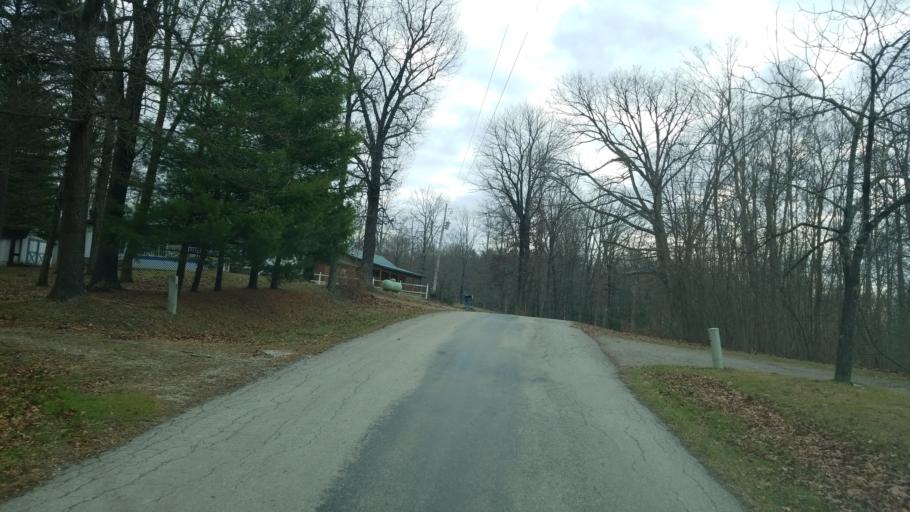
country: US
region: Ohio
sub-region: Highland County
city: Greenfield
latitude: 39.1783
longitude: -83.2687
